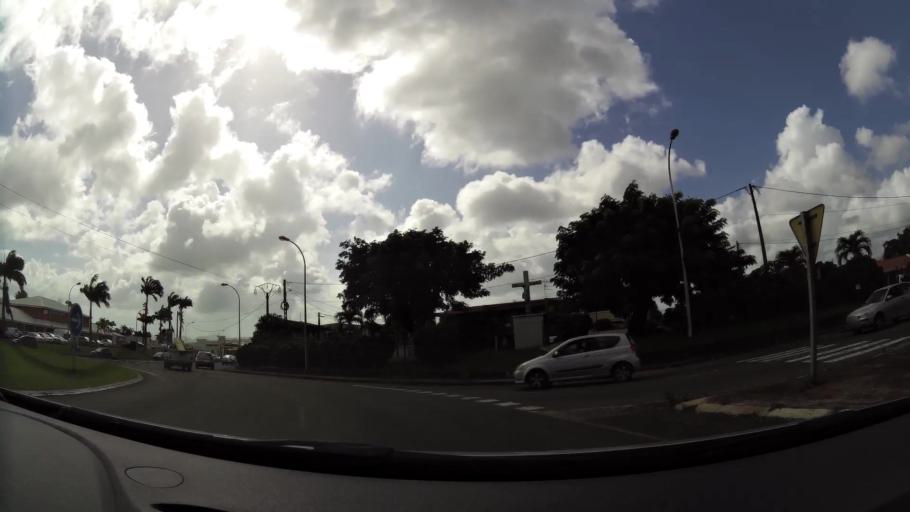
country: MQ
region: Martinique
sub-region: Martinique
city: Le Lamentin
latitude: 14.6236
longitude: -60.9892
